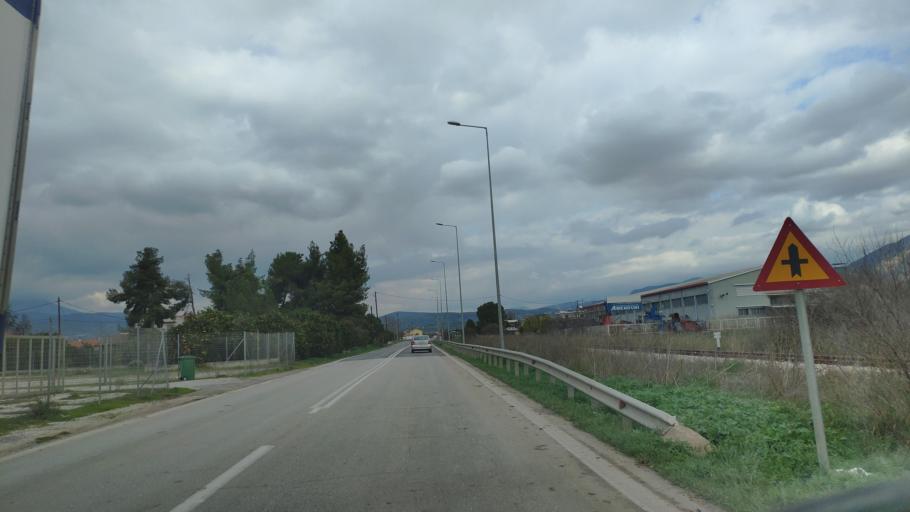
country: GR
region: Peloponnese
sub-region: Nomos Argolidos
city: Koutsopodi
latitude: 37.6814
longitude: 22.7192
